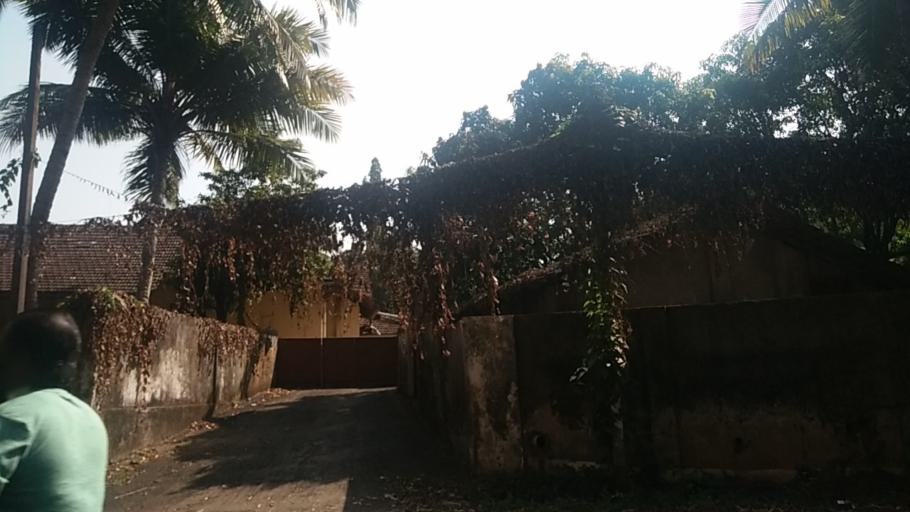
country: IN
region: Goa
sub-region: South Goa
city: Colva
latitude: 15.3216
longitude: 73.9061
